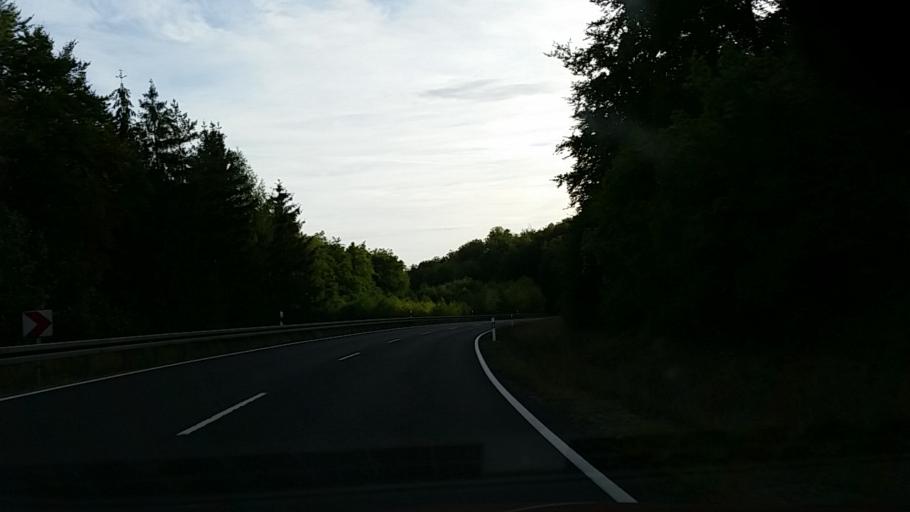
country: DE
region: Thuringia
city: Henneberg
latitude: 50.4745
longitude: 10.3295
